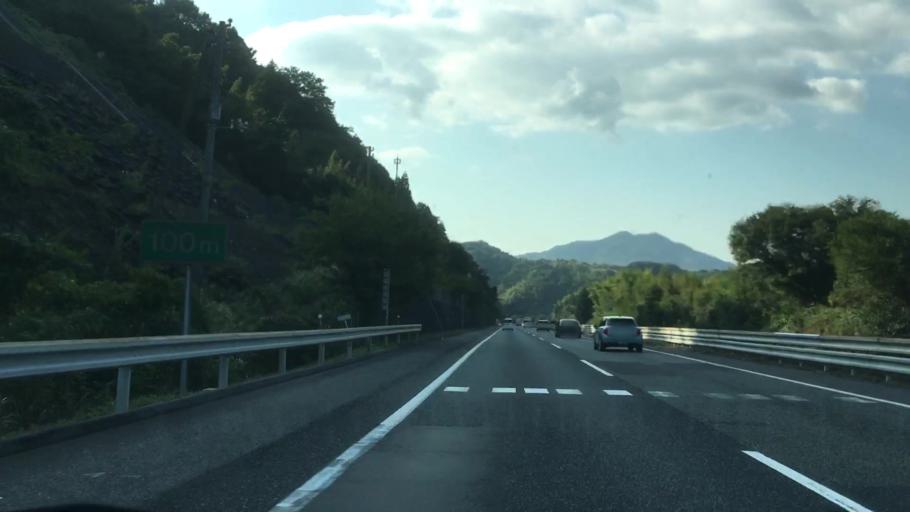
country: JP
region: Yamaguchi
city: Tokuyama
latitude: 34.0750
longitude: 131.8038
